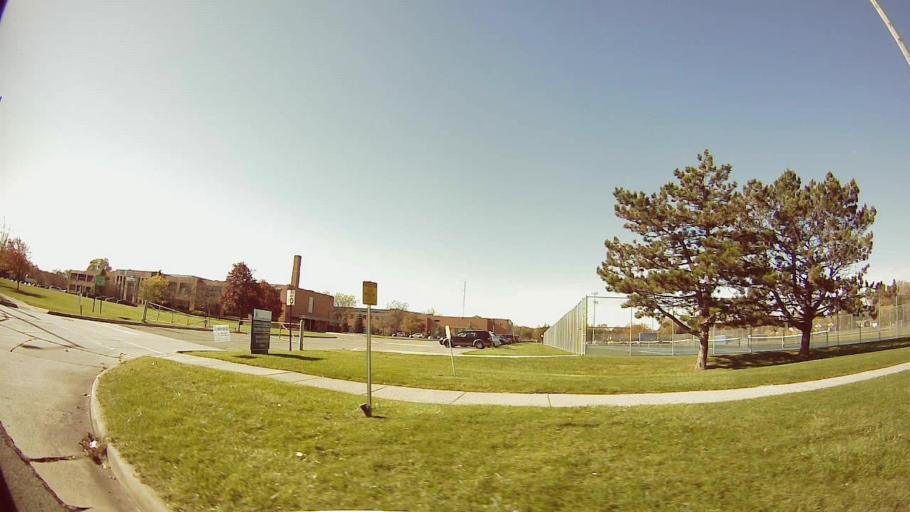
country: US
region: Michigan
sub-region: Oakland County
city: Southfield
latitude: 42.4708
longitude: -83.2609
